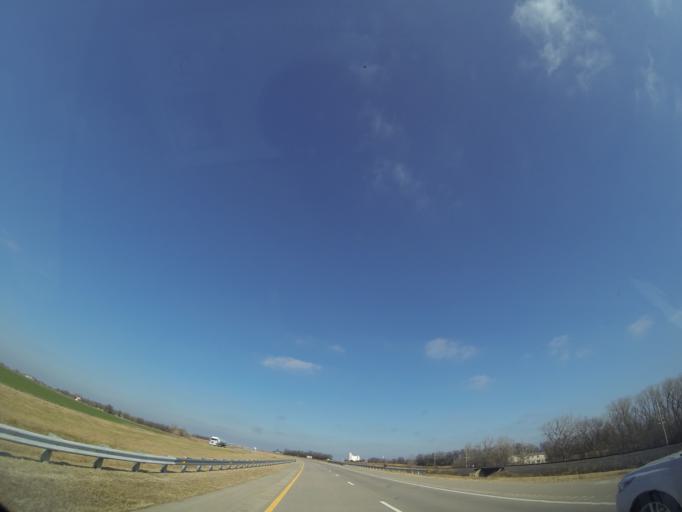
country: US
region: Kansas
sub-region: McPherson County
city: Inman
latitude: 38.2195
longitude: -97.7876
